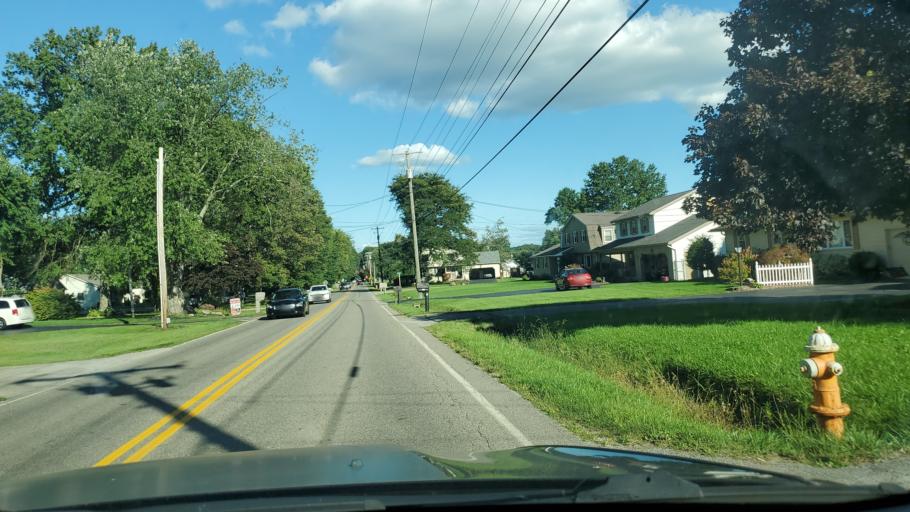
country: US
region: Ohio
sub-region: Mahoning County
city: Boardman
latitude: 41.0468
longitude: -80.7027
